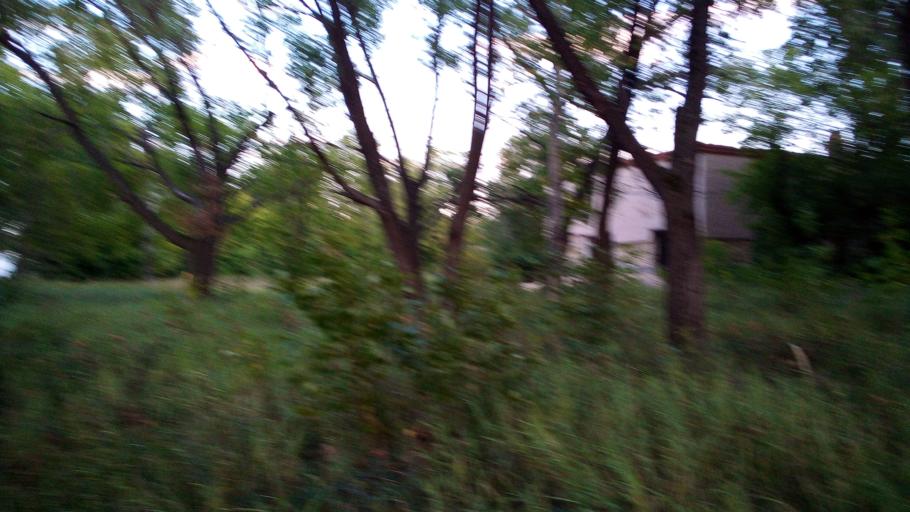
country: RU
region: Chelyabinsk
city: Potanino
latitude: 55.2899
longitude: 61.5119
